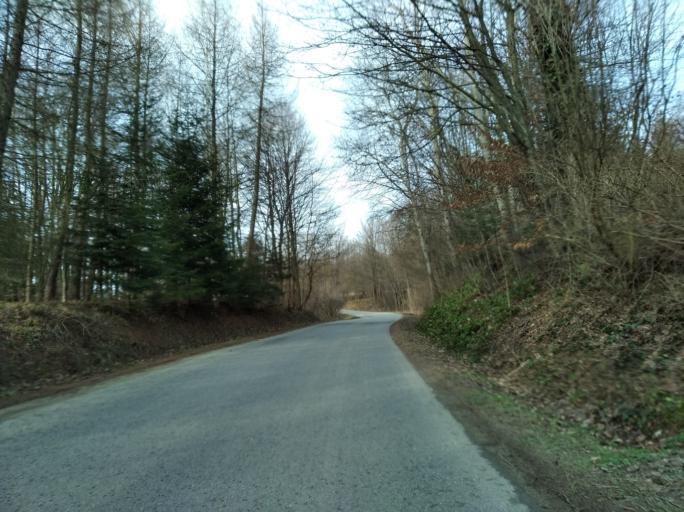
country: PL
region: Subcarpathian Voivodeship
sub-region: Powiat brzozowski
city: Turze Pole
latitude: 49.6738
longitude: 22.0036
